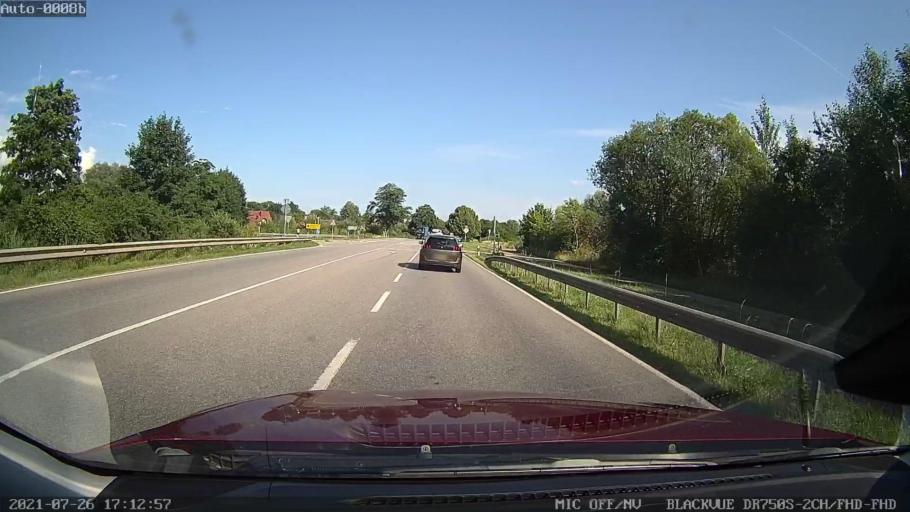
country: DE
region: Bavaria
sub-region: Upper Palatinate
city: Riekofen
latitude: 48.9731
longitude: 12.3111
